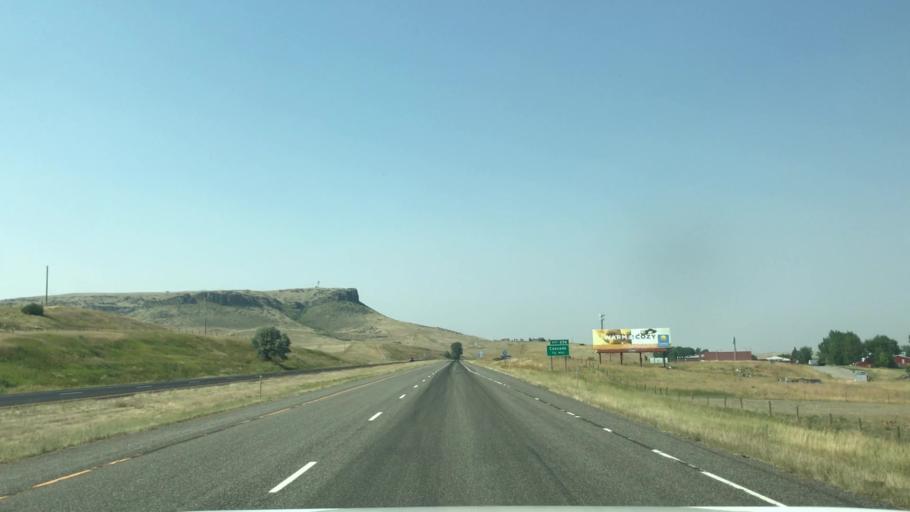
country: US
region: Montana
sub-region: Cascade County
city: Sun Prairie
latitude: 47.2661
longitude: -111.7079
